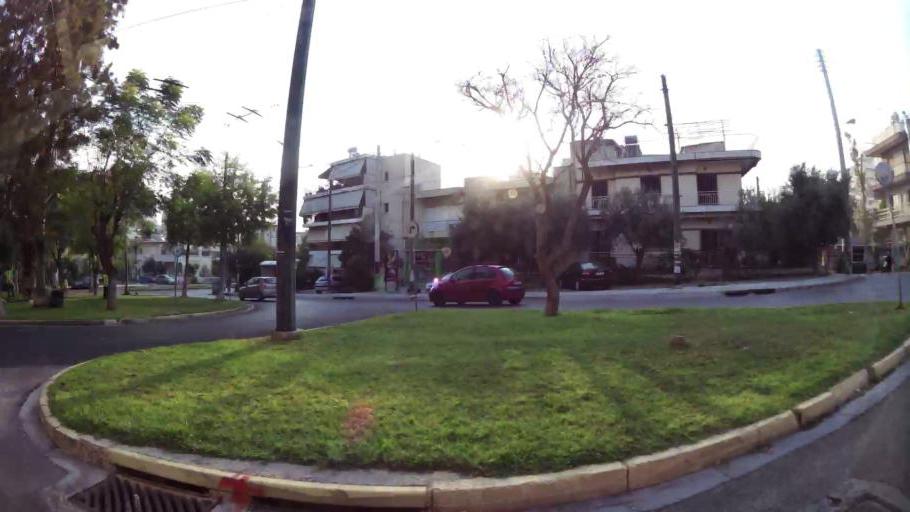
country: GR
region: Attica
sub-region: Nomarchia Athinas
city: Petroupolis
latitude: 38.0397
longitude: 23.6793
